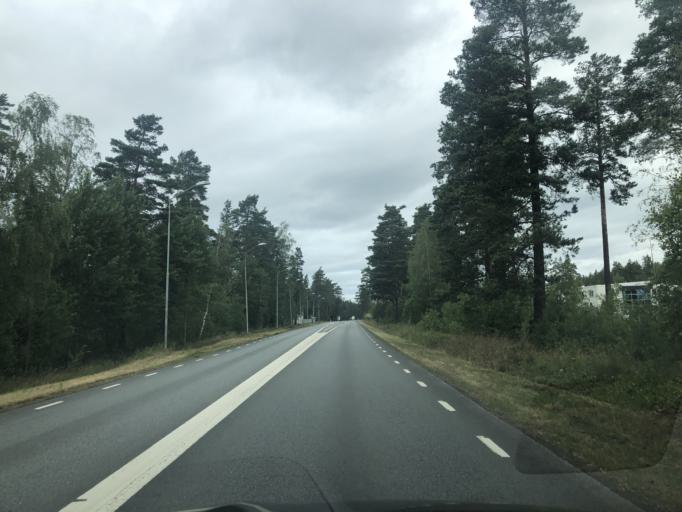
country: SE
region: Joenkoeping
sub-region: Vaggeryds Kommun
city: Vaggeryd
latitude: 57.5101
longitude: 14.1416
